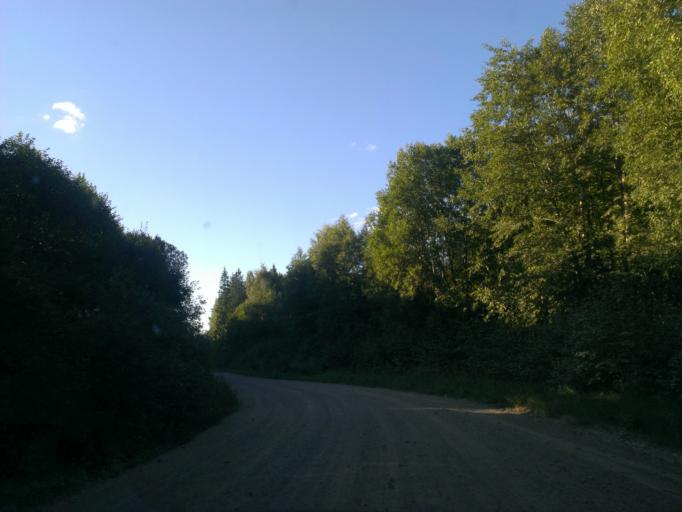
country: LV
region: Malpils
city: Malpils
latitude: 57.0910
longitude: 25.0499
